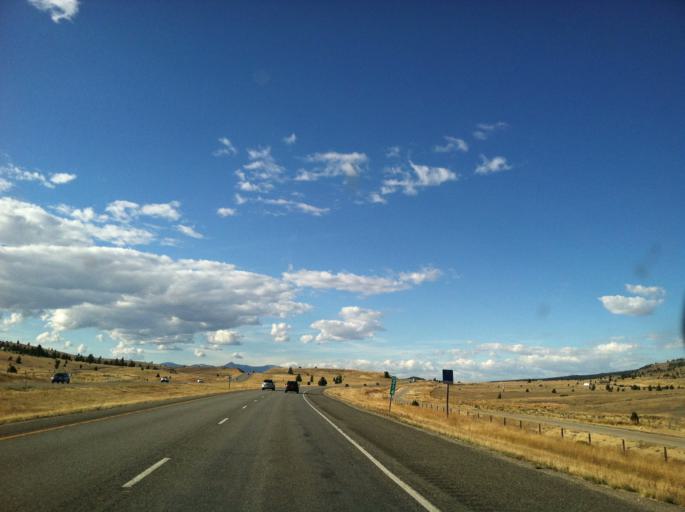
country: US
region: Montana
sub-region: Silver Bow County
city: Butte-Silver Bow (Balance)
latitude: 46.0294
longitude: -112.7309
